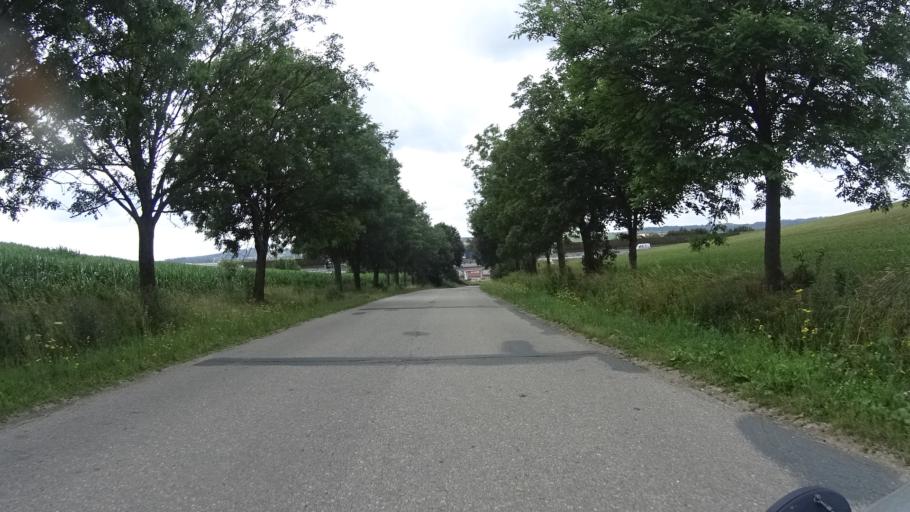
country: CZ
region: Vysocina
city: Merin
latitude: 49.3943
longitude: 15.8986
